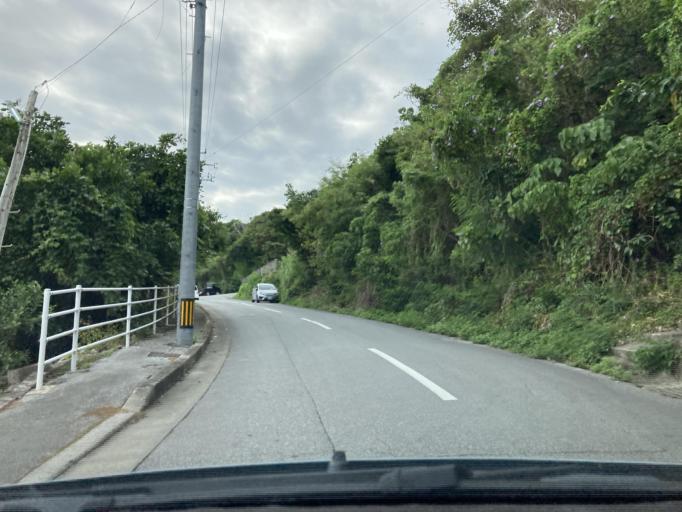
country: JP
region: Okinawa
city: Tomigusuku
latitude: 26.1353
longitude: 127.7898
